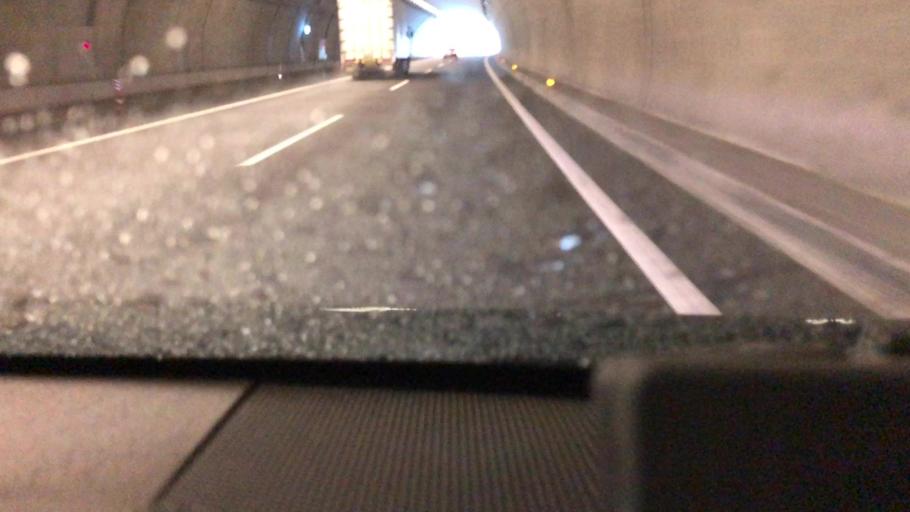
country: JP
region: Shizuoka
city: Fujinomiya
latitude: 35.1844
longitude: 138.6145
